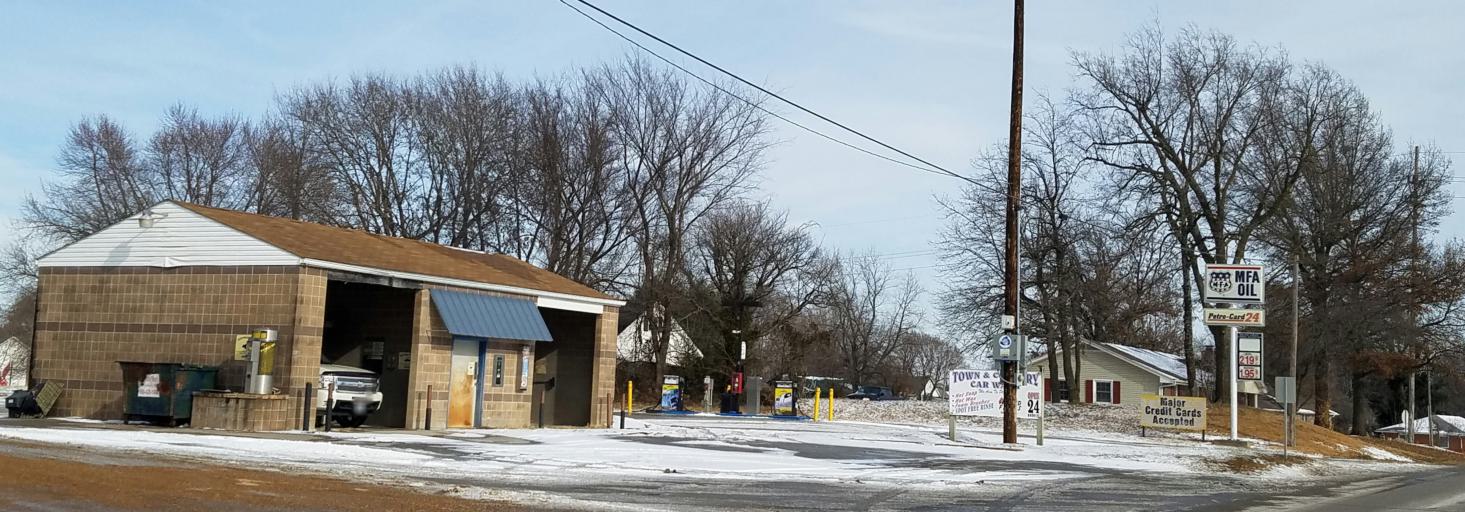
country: US
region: Missouri
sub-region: Carroll County
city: Carrollton
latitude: 39.2070
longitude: -93.5244
